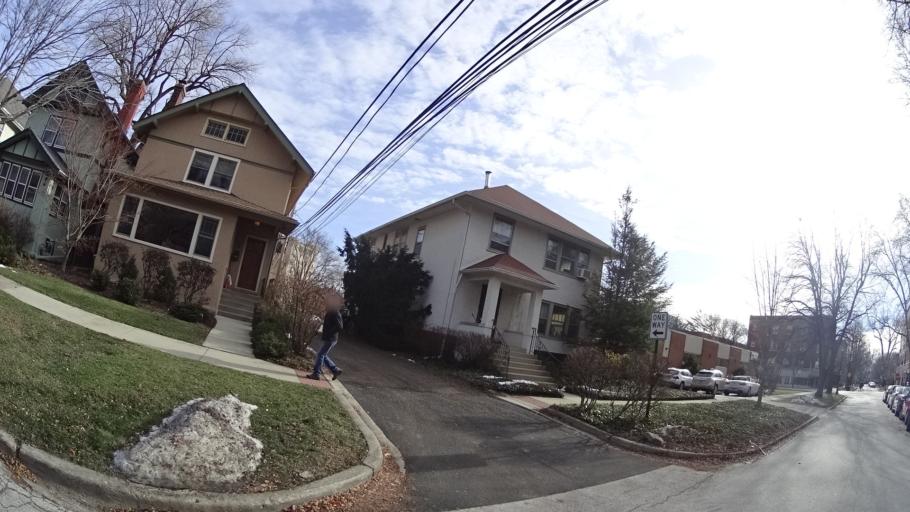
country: US
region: Illinois
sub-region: Cook County
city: Evanston
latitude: 42.0649
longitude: -87.6956
